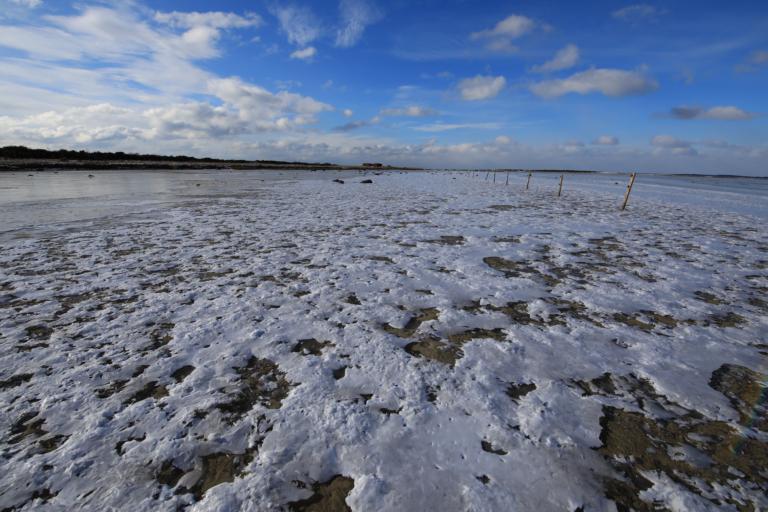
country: SE
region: Halland
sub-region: Varbergs Kommun
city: Varberg
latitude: 57.1286
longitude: 12.2169
